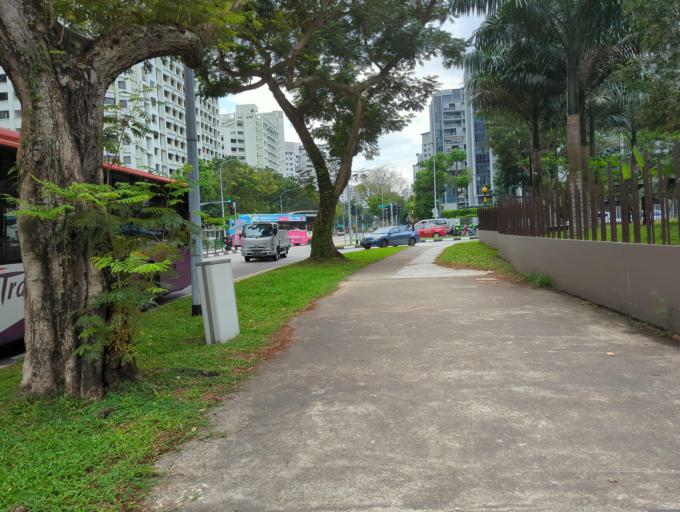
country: MY
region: Johor
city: Kampung Pasir Gudang Baru
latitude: 1.3904
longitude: 103.8974
